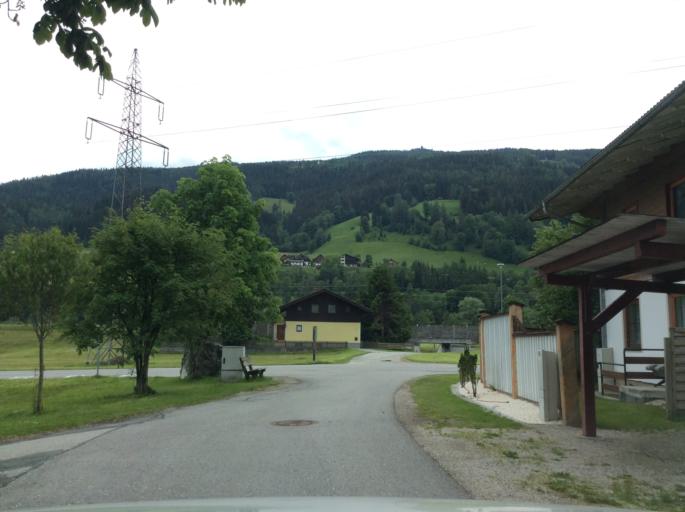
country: AT
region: Styria
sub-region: Politischer Bezirk Liezen
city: Schladming
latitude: 47.4039
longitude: 13.7100
